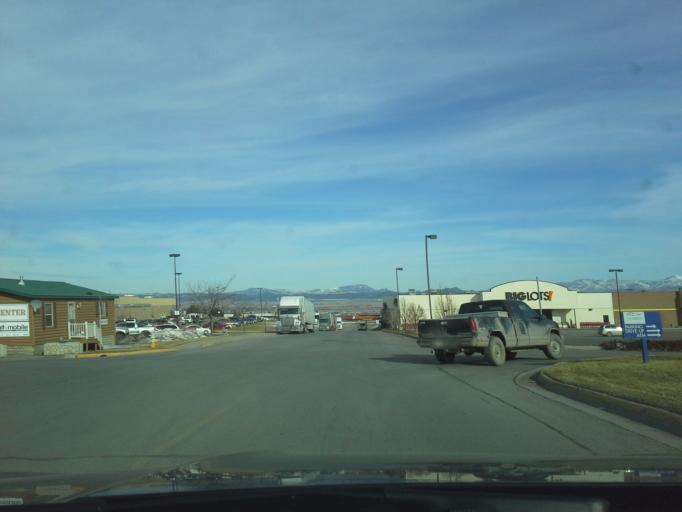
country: US
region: Montana
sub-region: Lewis and Clark County
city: Helena
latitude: 46.5919
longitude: -111.9887
